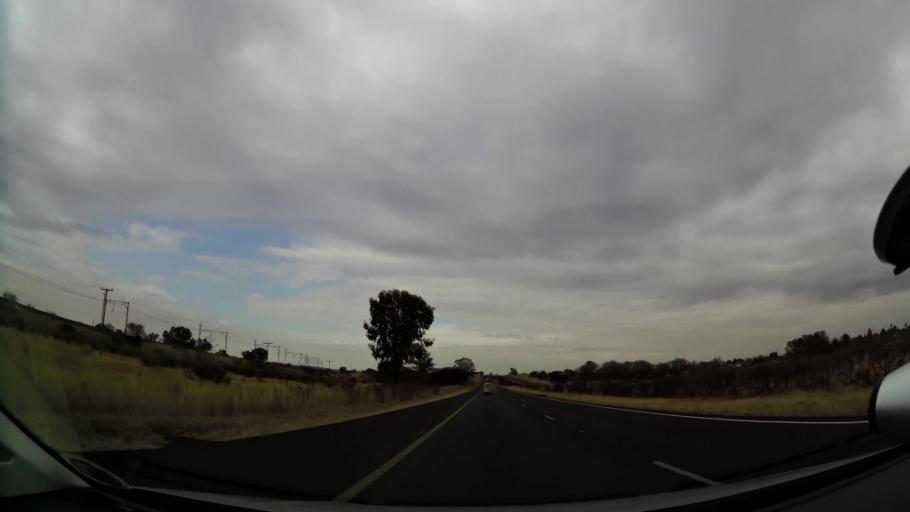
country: ZA
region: Orange Free State
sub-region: Fezile Dabi District Municipality
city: Kroonstad
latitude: -27.6323
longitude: 27.2503
